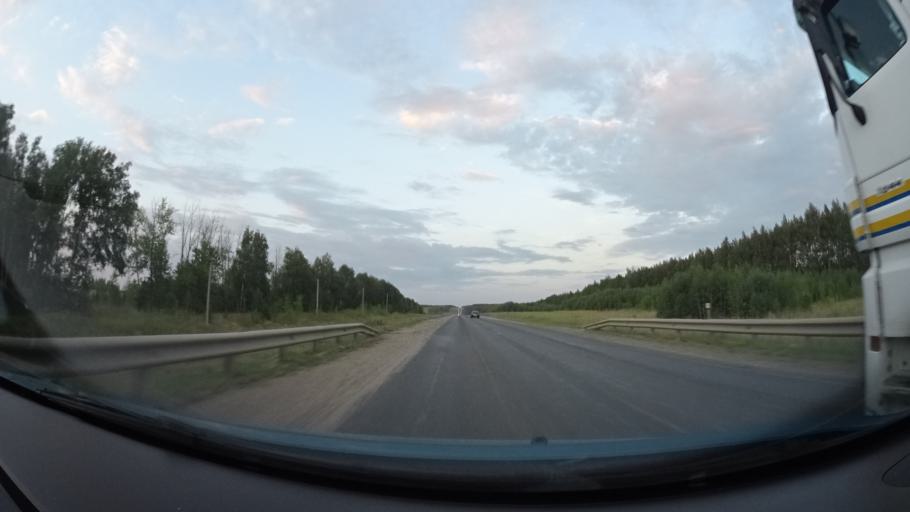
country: RU
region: Tatarstan
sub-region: Bugul'minskiy Rayon
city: Bugul'ma
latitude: 54.2596
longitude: 52.9046
